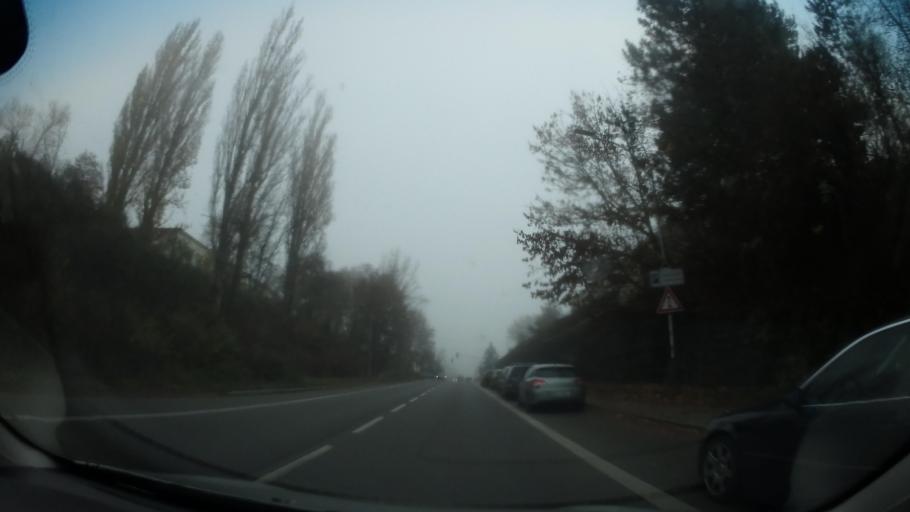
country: CZ
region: South Moravian
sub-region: Okres Hodonin
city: Kyjov
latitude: 49.0067
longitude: 17.1086
